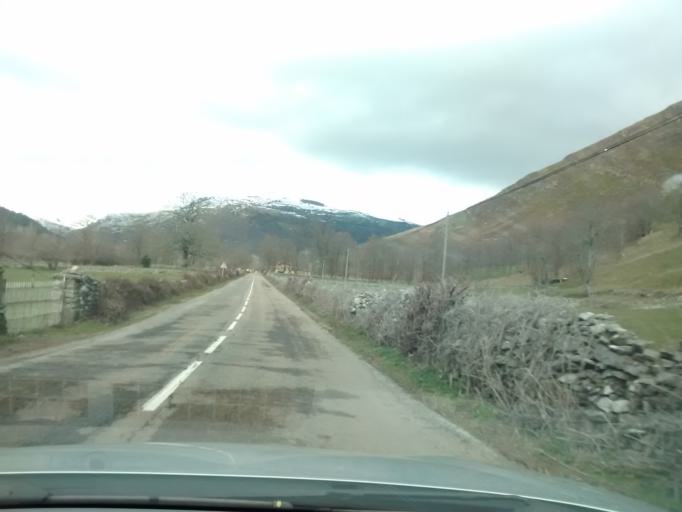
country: ES
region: Castille and Leon
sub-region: Provincia de Burgos
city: Espinosa de los Monteros
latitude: 43.1040
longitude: -3.5719
